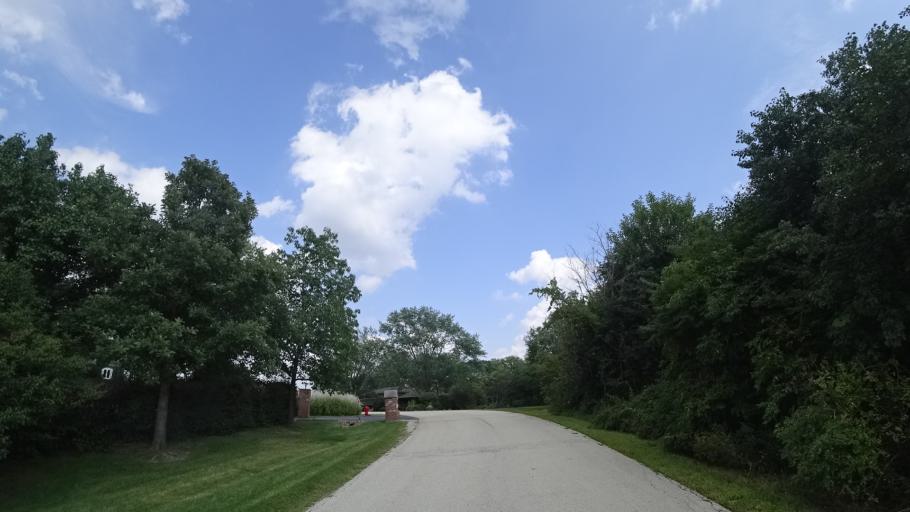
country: US
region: Illinois
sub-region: Will County
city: Goodings Grove
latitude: 41.6552
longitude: -87.8952
